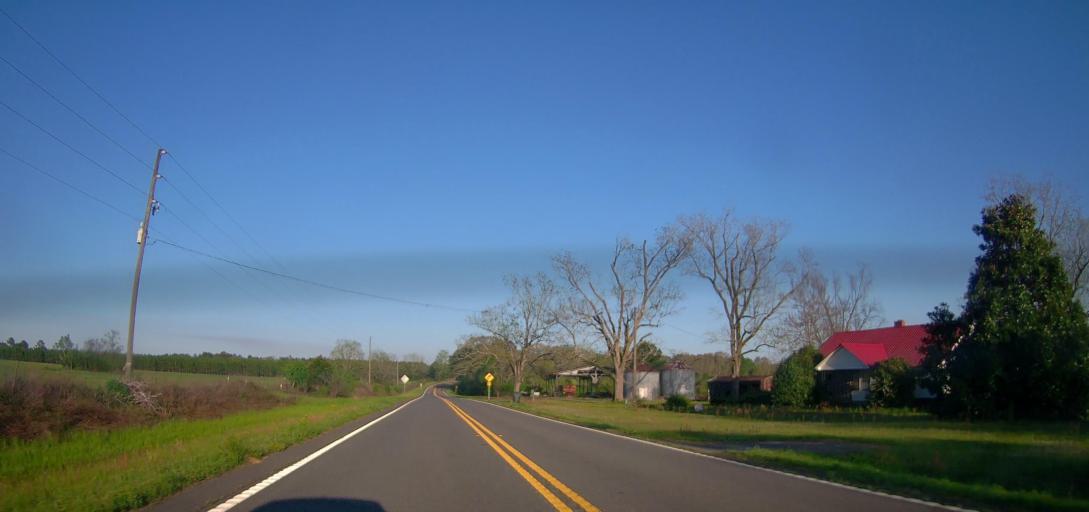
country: US
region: Georgia
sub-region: Schley County
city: Ellaville
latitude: 32.3438
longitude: -84.3619
